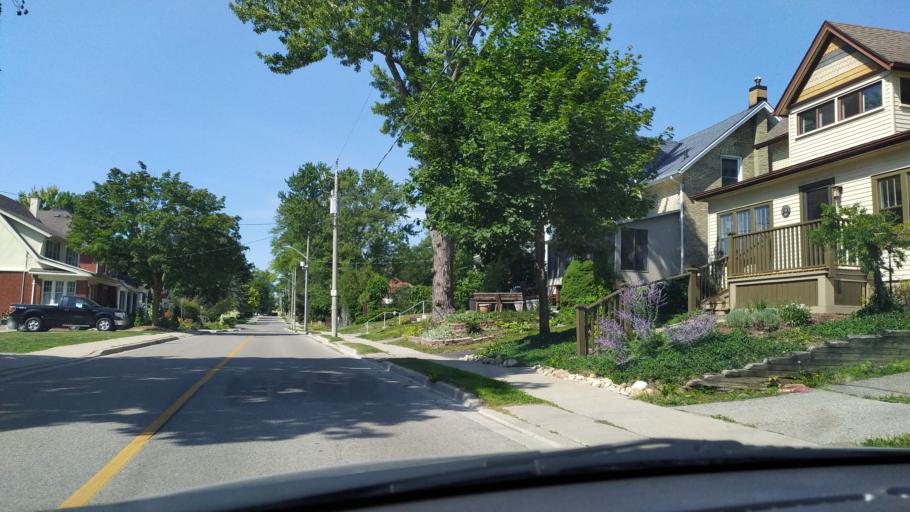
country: CA
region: Ontario
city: Stratford
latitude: 43.3756
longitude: -80.9782
